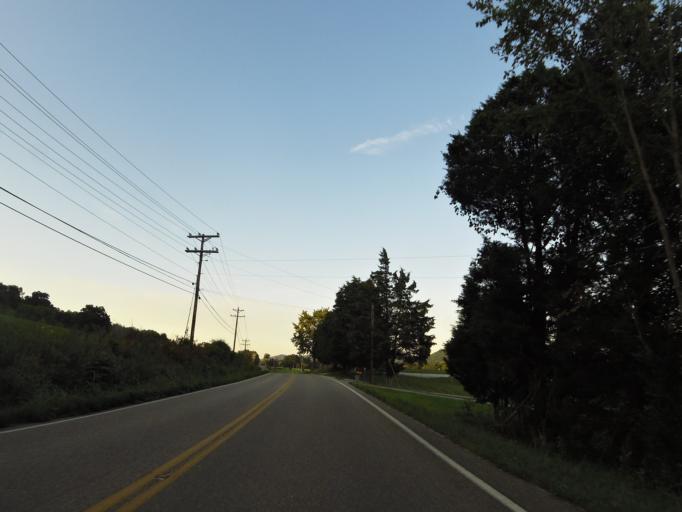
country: US
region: Tennessee
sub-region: Roane County
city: Rockwood
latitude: 35.7440
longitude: -84.6179
